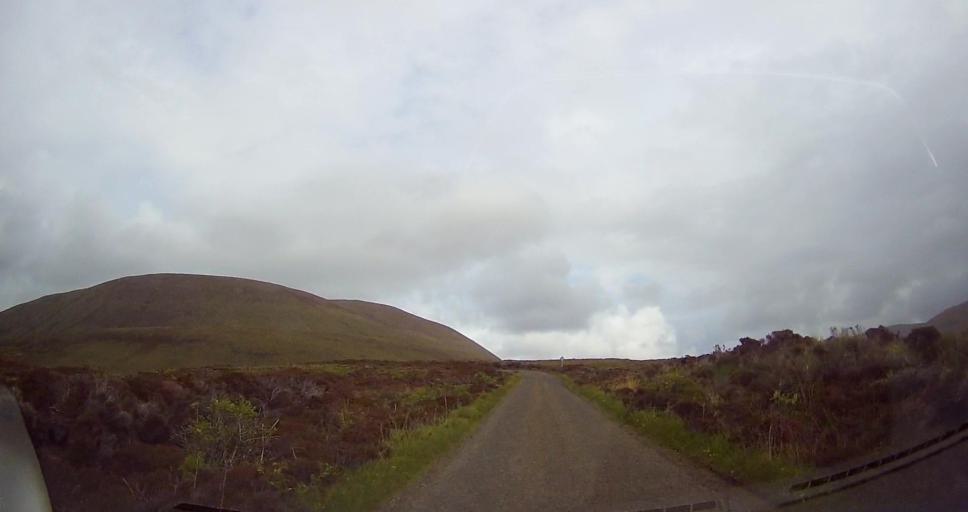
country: GB
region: Scotland
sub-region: Orkney Islands
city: Stromness
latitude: 58.8801
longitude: -3.3849
